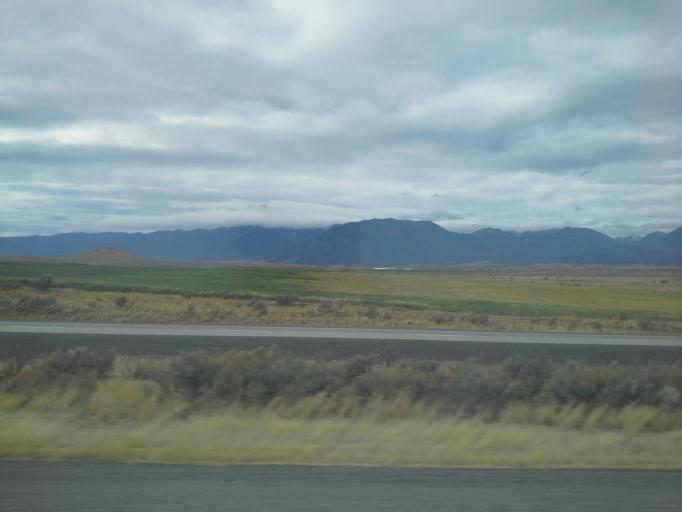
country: US
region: Oregon
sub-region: Baker County
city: Baker City
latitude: 44.9686
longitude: -117.8744
